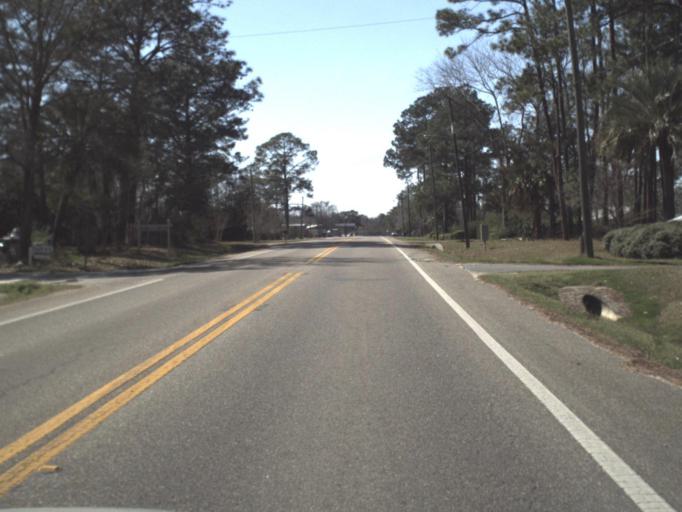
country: US
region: Florida
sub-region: Calhoun County
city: Blountstown
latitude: 30.4522
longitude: -85.0507
